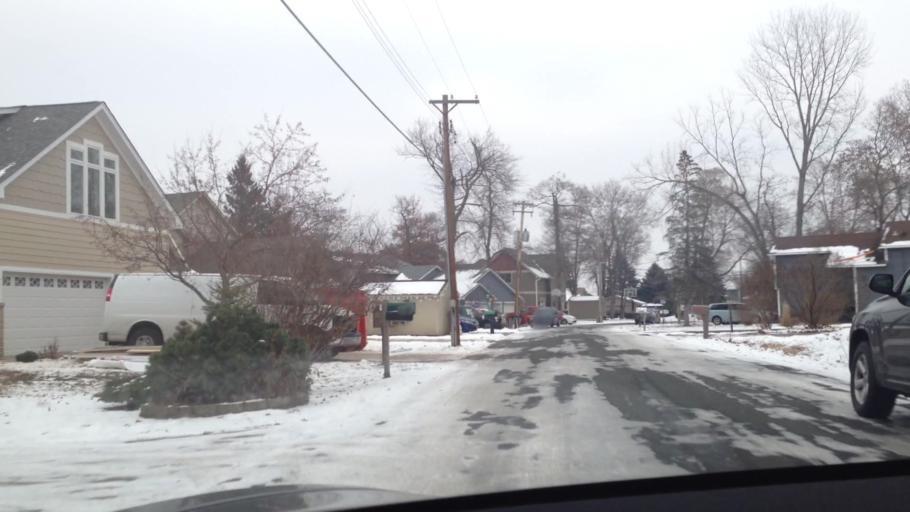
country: US
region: Minnesota
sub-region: Washington County
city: Forest Lake
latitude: 45.2670
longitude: -92.9404
